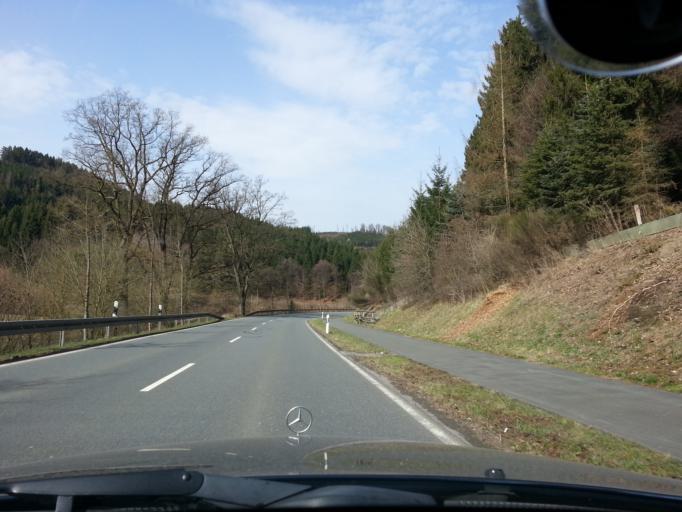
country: DE
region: North Rhine-Westphalia
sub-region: Regierungsbezirk Arnsberg
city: Bad Fredeburg
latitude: 51.2754
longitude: 8.3491
